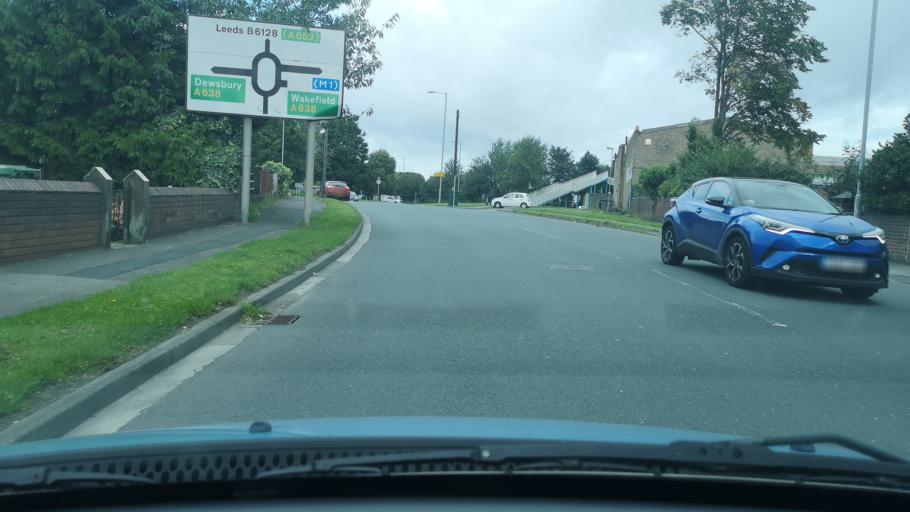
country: GB
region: England
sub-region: City and Borough of Wakefield
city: Ossett
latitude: 53.6922
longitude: -1.5903
